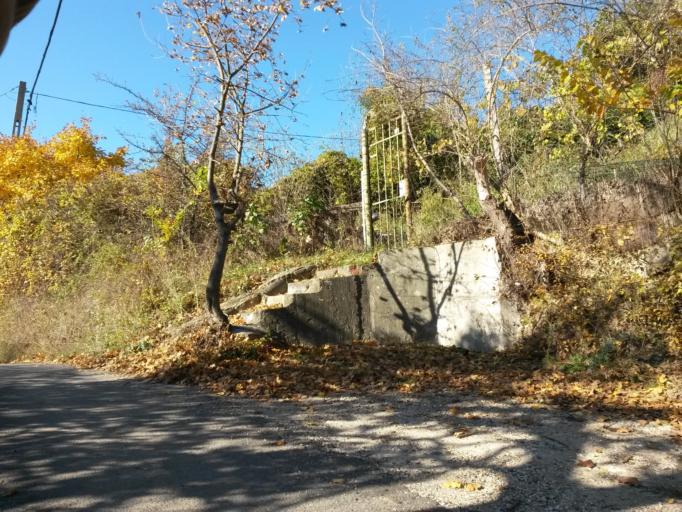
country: HU
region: Pest
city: Budaors
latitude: 47.4756
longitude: 18.9635
